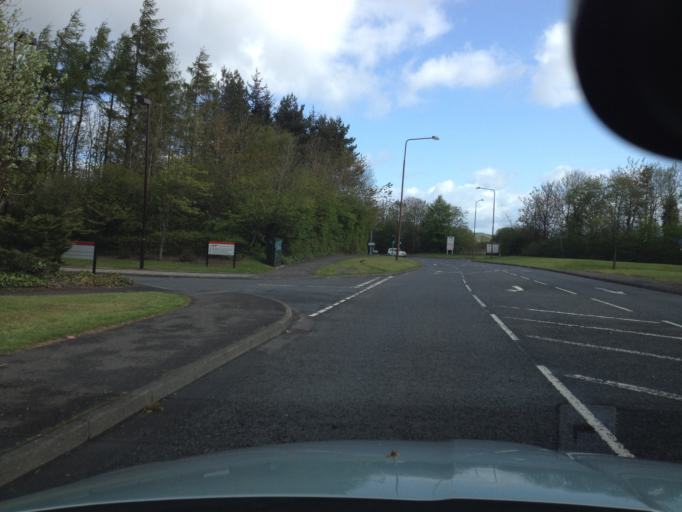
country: GB
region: Scotland
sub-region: West Lothian
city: Livingston
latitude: 55.8792
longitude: -3.5399
